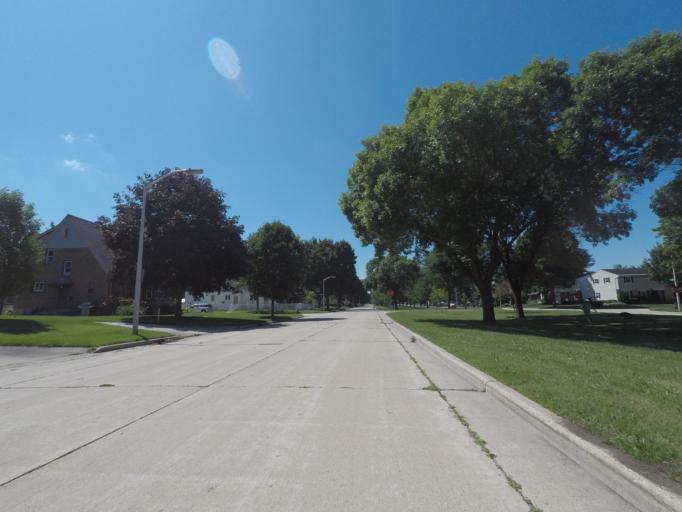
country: US
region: Wisconsin
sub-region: Waukesha County
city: Elm Grove
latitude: 43.0223
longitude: -88.0619
